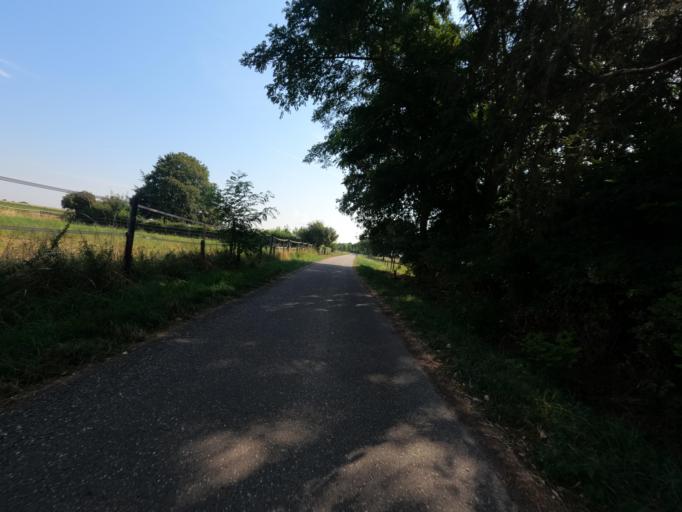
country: DE
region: North Rhine-Westphalia
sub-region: Regierungsbezirk Koln
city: Titz
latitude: 51.0025
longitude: 6.3496
